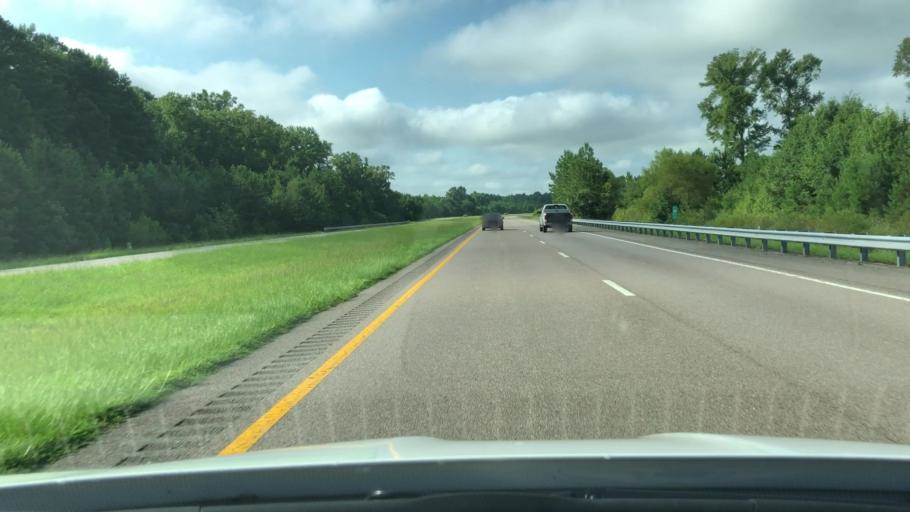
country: US
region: Virginia
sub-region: City of Portsmouth
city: Portsmouth Heights
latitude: 36.6580
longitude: -76.3545
